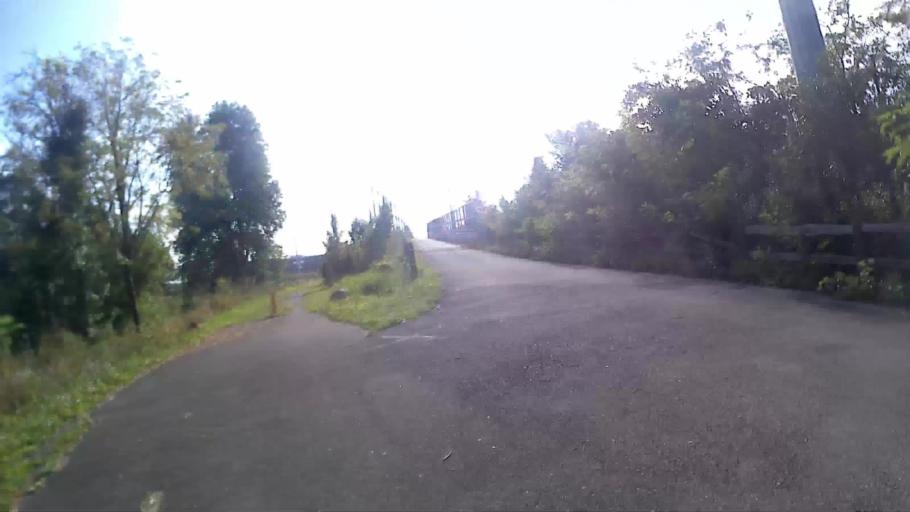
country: US
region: Illinois
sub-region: DuPage County
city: Warrenville
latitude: 41.8114
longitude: -88.2061
